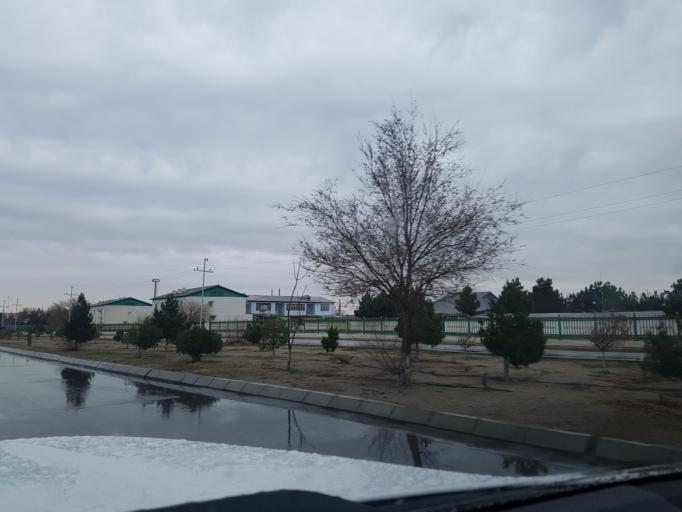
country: TM
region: Balkan
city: Balkanabat
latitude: 39.5096
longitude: 54.3467
